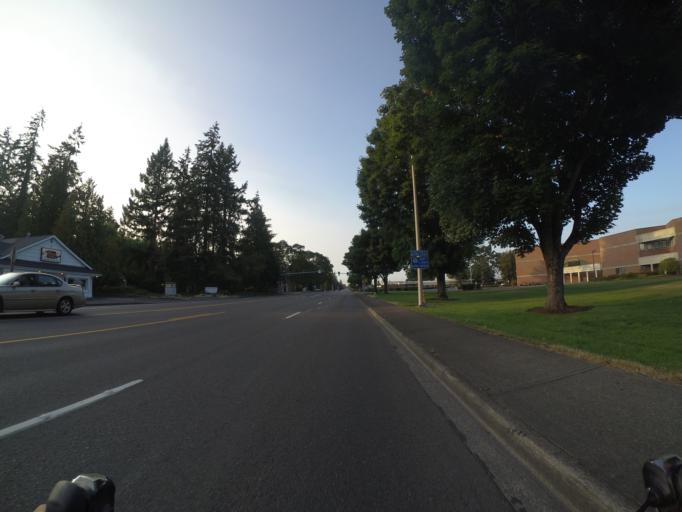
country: US
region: Washington
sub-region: Pierce County
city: Lakewood
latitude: 47.1572
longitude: -122.5204
